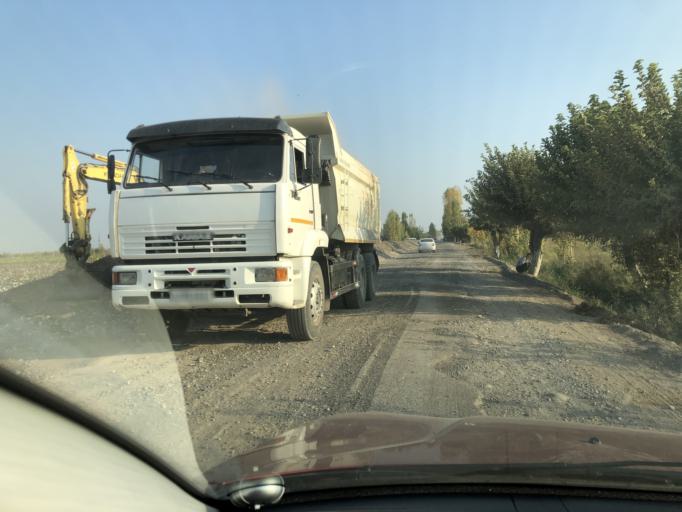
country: UZ
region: Namangan
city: Uychi
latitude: 41.0671
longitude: 71.9849
